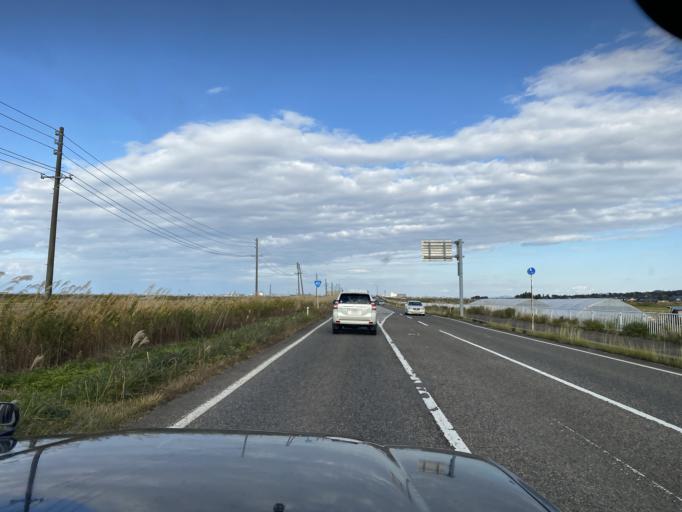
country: JP
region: Niigata
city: Niitsu-honcho
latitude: 37.7737
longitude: 139.1046
